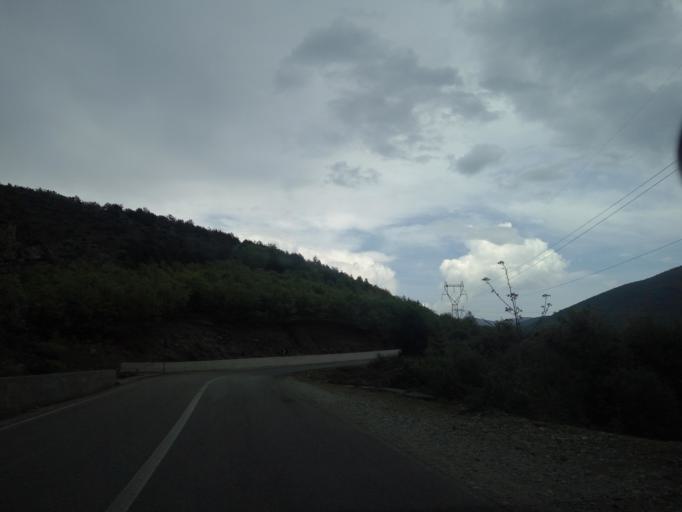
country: AL
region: Kukes
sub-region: Rrethi i Tropojes
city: Llugaj
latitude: 42.3849
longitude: 20.1432
